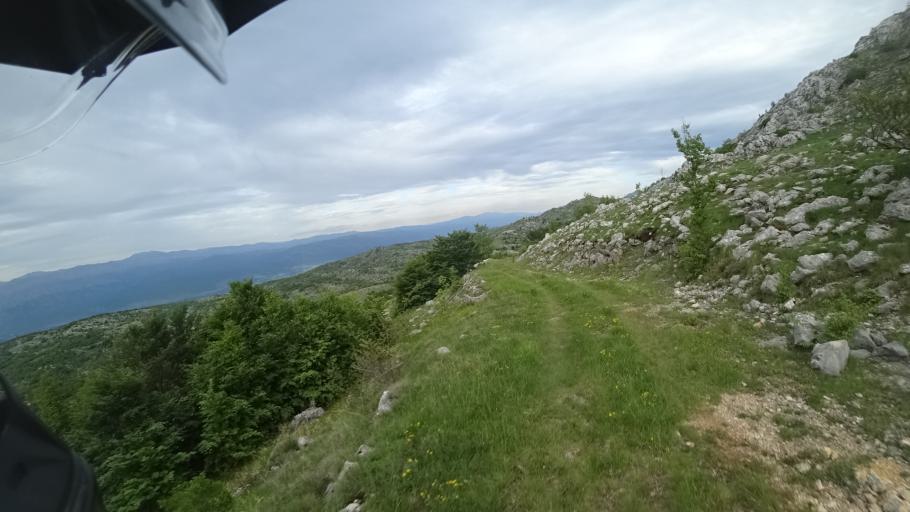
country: HR
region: Sibensko-Kniniska
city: Drnis
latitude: 43.8588
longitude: 16.3826
